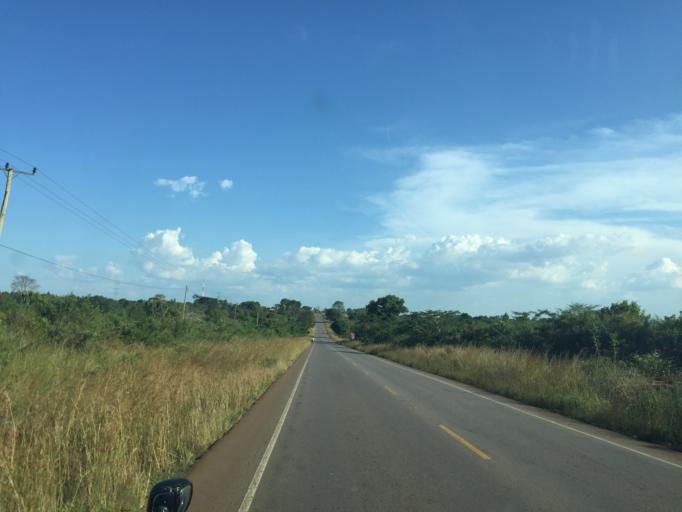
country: UG
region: Central Region
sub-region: Nakasongola District
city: Nakasongola
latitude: 1.2583
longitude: 32.4531
